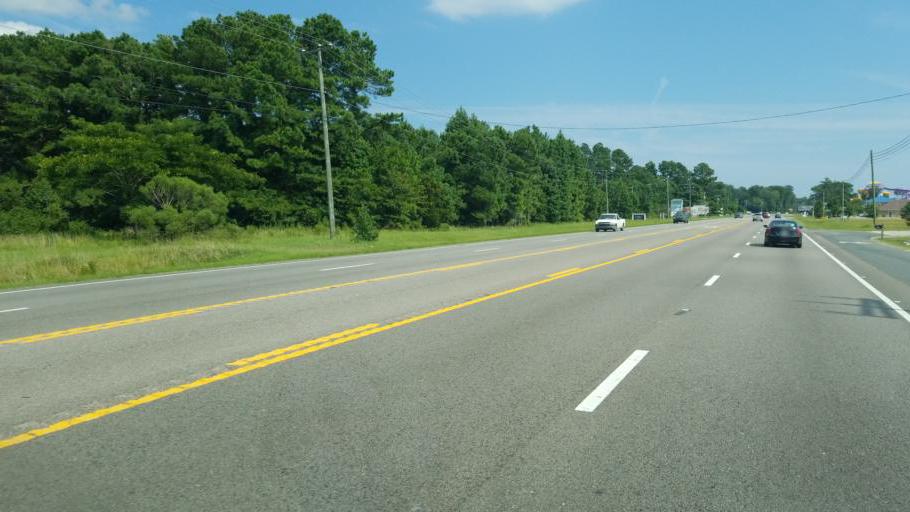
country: US
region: North Carolina
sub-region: Dare County
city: Southern Shores
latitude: 36.1180
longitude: -75.8310
